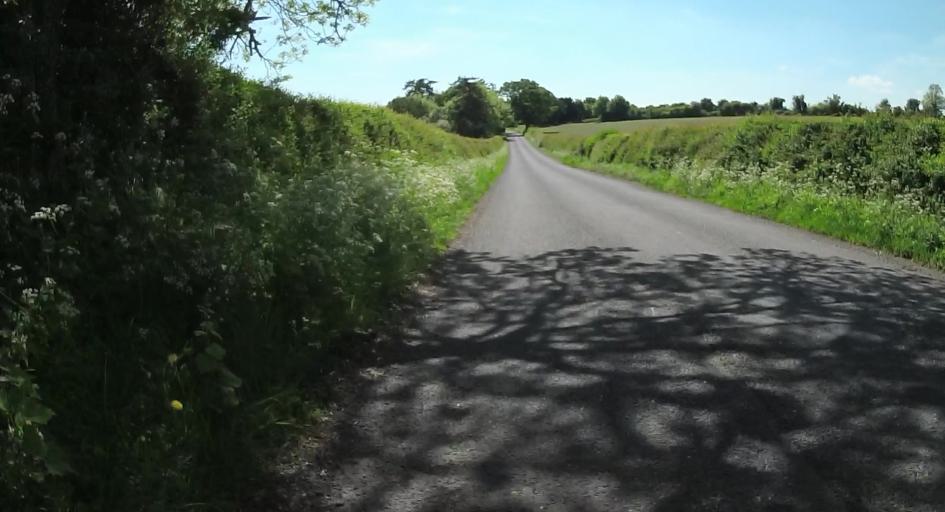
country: GB
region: England
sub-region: Hampshire
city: Four Marks
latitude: 51.1473
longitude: -1.1486
